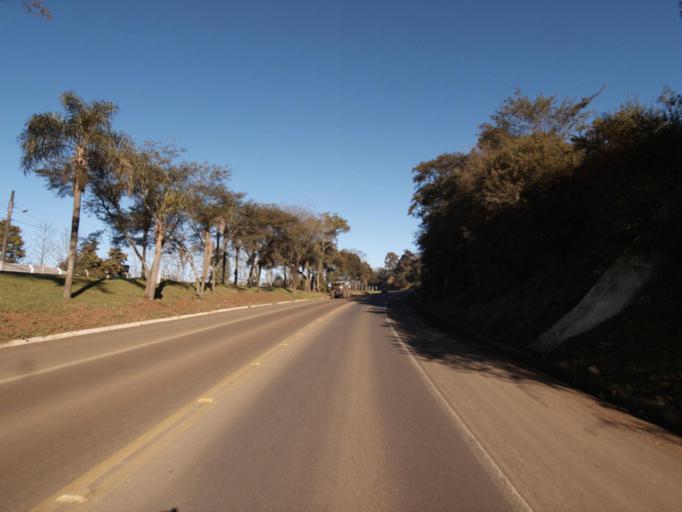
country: BR
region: Rio Grande do Sul
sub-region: Frederico Westphalen
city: Frederico Westphalen
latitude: -26.8909
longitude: -53.1831
